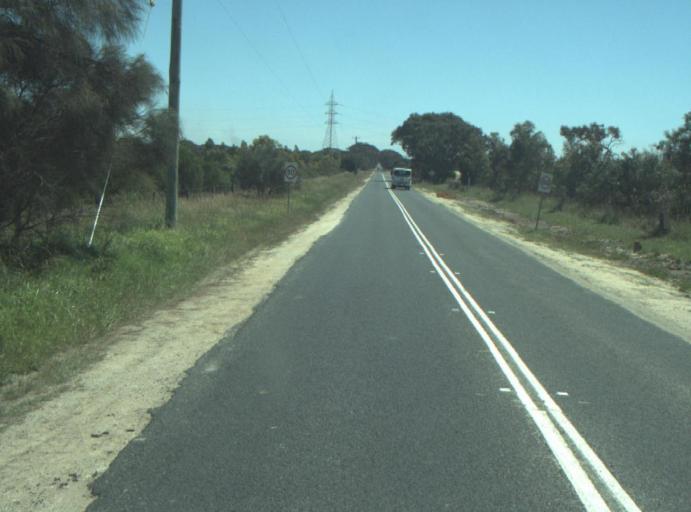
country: AU
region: Victoria
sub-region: Greater Geelong
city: Breakwater
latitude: -38.2501
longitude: 144.3509
